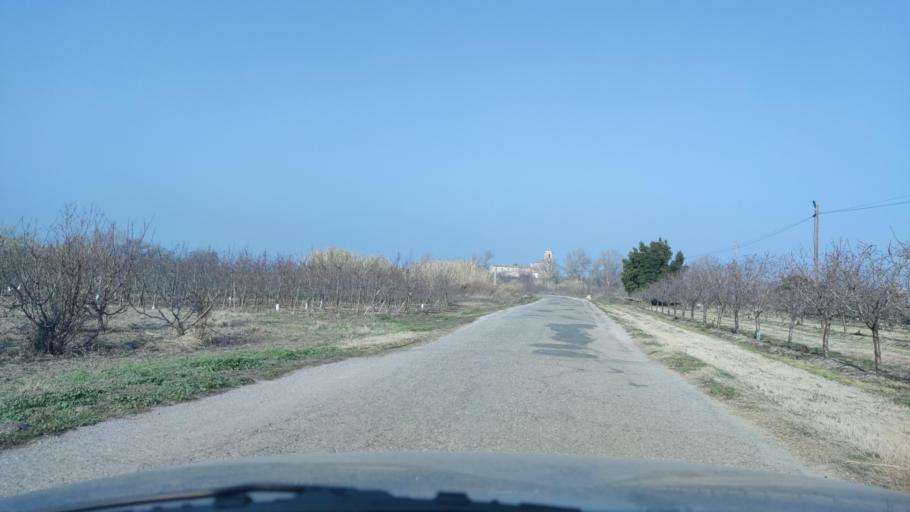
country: ES
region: Catalonia
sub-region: Provincia de Lleida
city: la Granja d'Escarp
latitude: 41.4270
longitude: 0.3551
